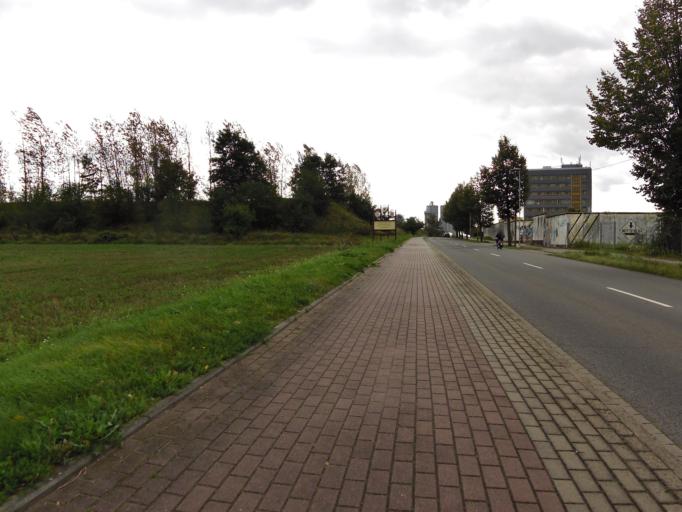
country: DE
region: Saxony-Anhalt
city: Tangermunde
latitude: 52.5627
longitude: 11.9803
